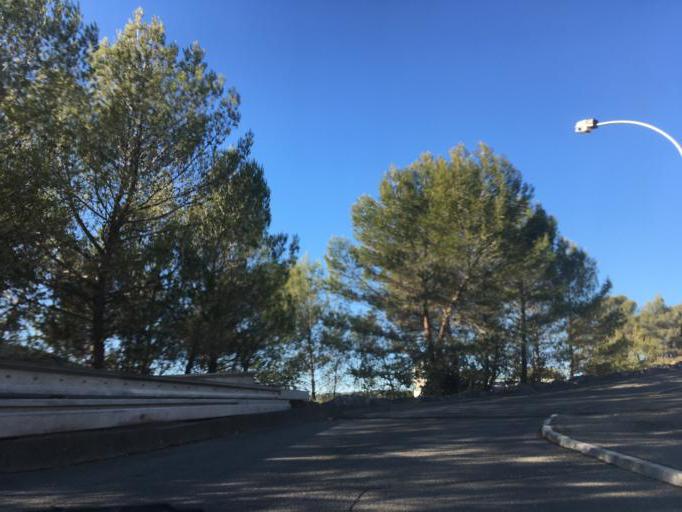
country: FR
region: Provence-Alpes-Cote d'Azur
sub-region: Departement du Var
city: Salernes
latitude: 43.5717
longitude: 6.2184
